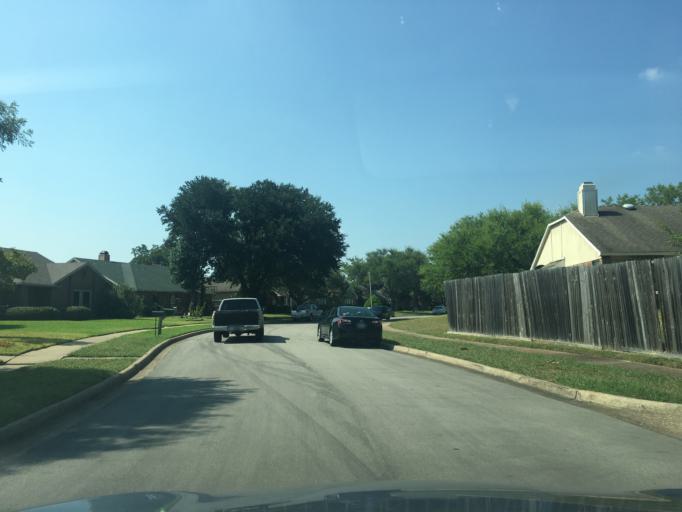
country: US
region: Texas
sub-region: Dallas County
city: Garland
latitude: 32.9452
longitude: -96.6265
